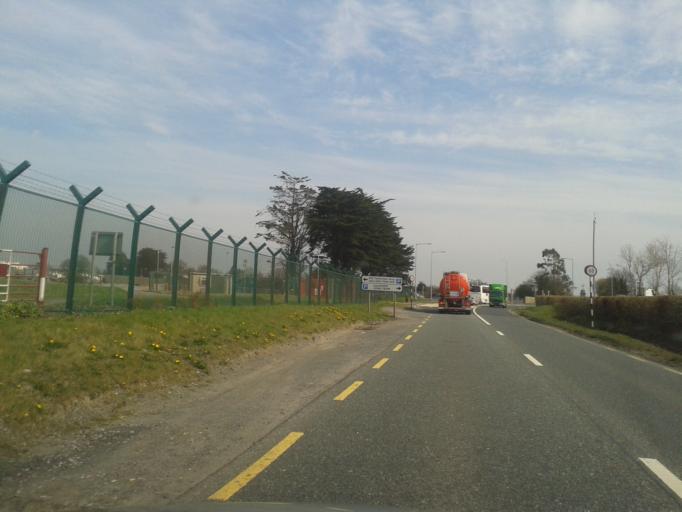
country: IE
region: Leinster
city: Beaumont
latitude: 53.4177
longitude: -6.2409
